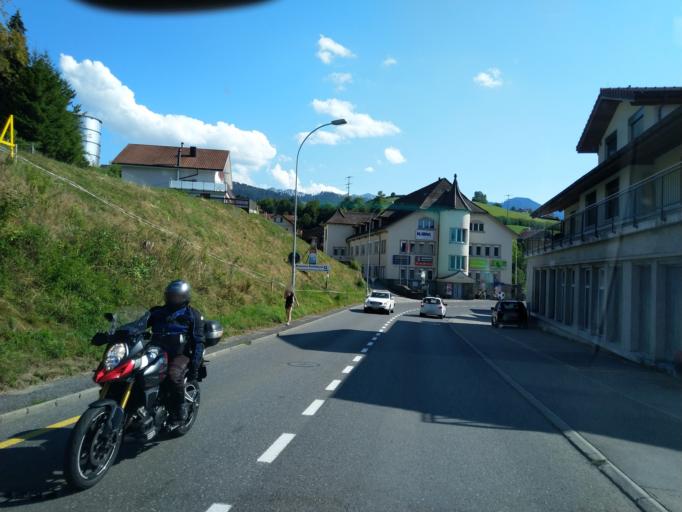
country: CH
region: Lucerne
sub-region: Entlebuch District
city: Entlebuch
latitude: 46.9854
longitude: 8.0613
